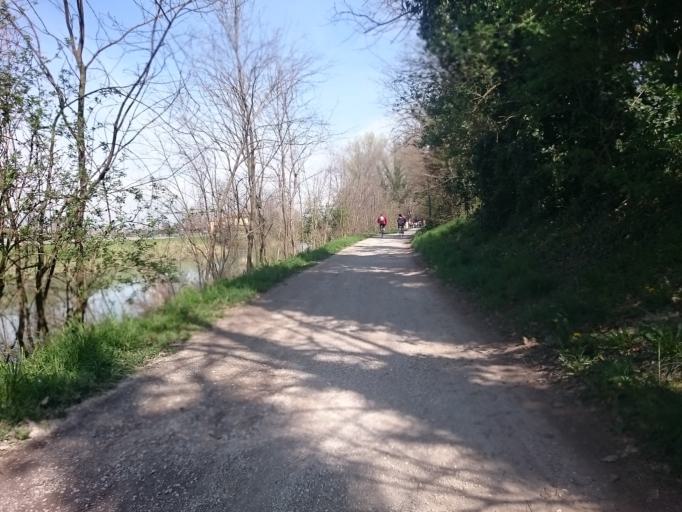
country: IT
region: Veneto
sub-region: Provincia di Padova
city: Limena
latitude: 45.4631
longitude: 11.8356
